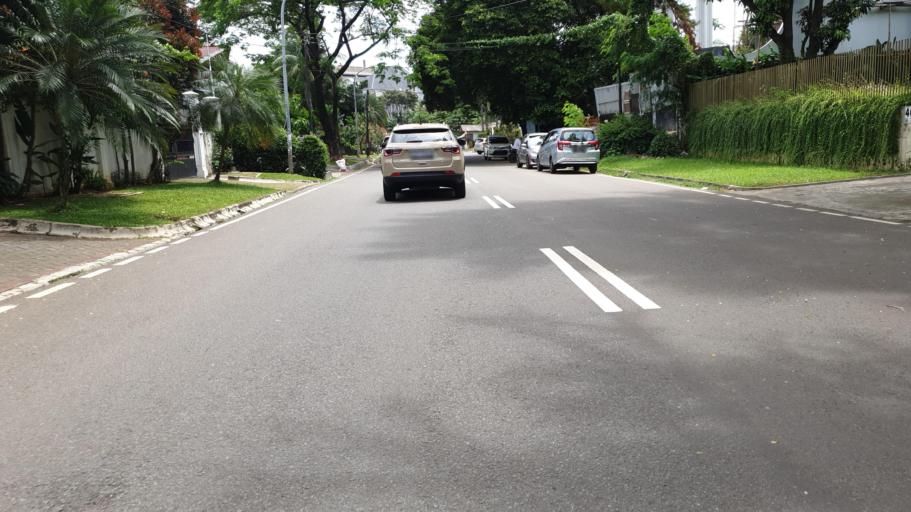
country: ID
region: Banten
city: South Tangerang
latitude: -6.2766
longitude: 106.7858
